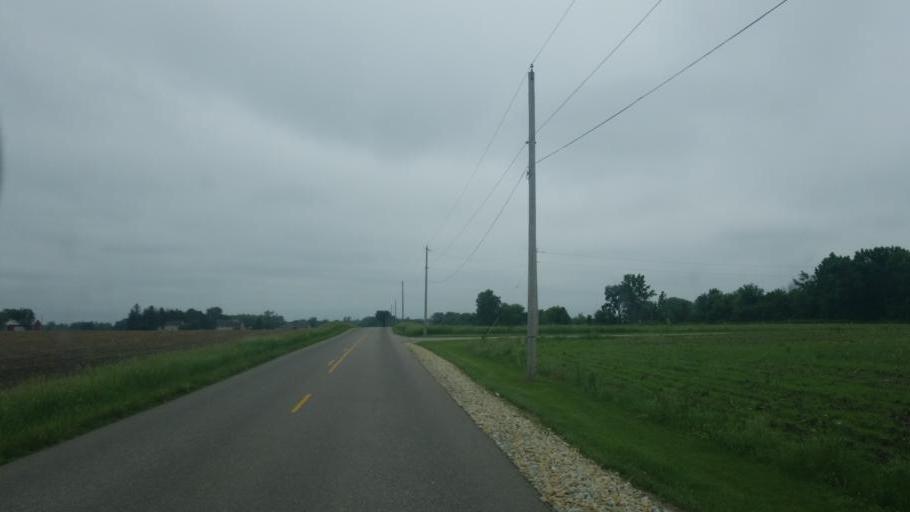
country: US
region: Indiana
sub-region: Elkhart County
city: Nappanee
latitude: 41.4627
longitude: -86.0207
